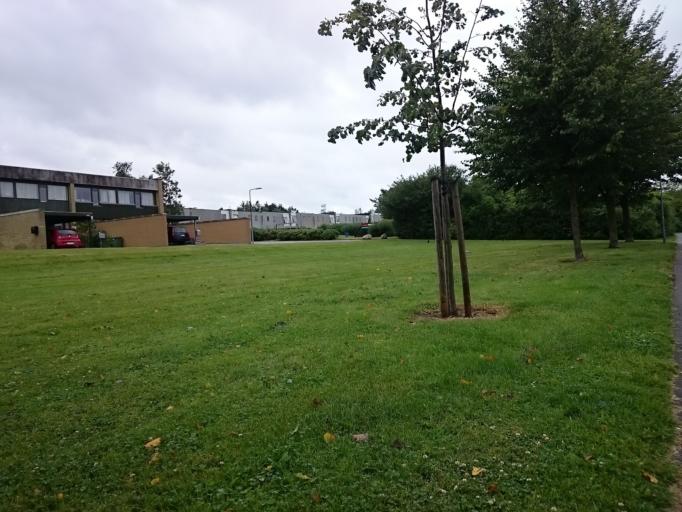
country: DK
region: Central Jutland
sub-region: Arhus Kommune
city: Stavtrup
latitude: 56.1230
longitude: 10.1372
